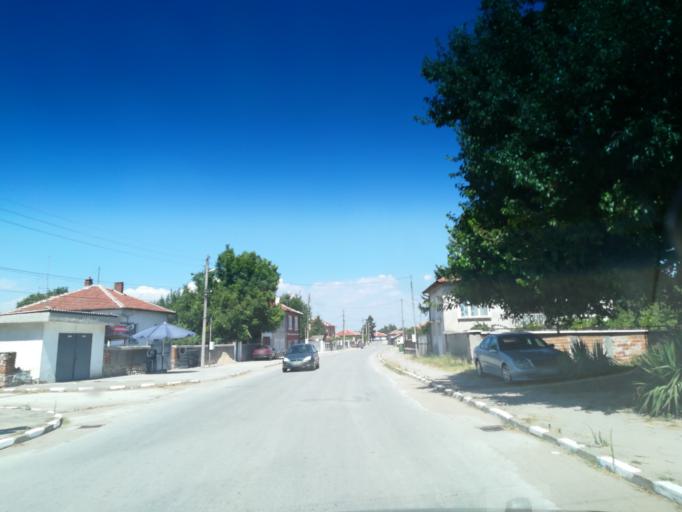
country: BG
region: Plovdiv
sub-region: Obshtina Sadovo
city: Sadovo
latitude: 42.0258
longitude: 25.1063
